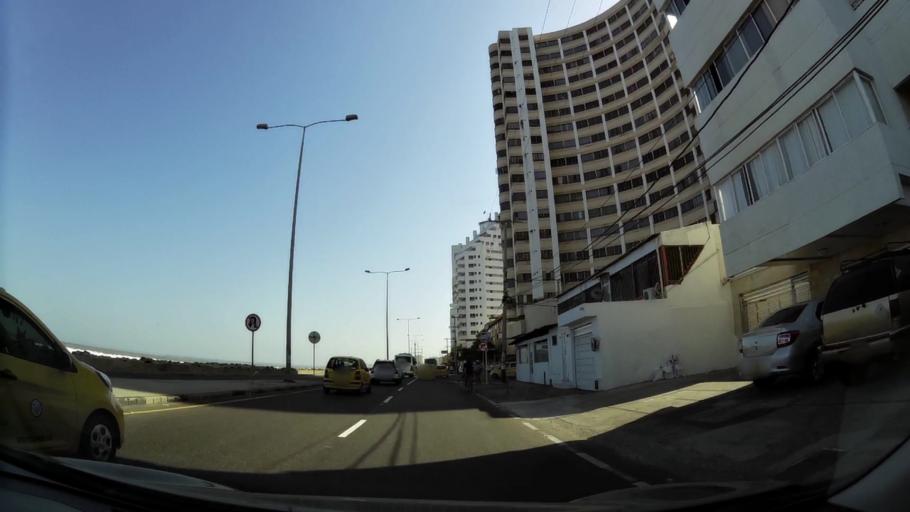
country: CO
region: Bolivar
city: Cartagena
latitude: 10.4355
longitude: -75.5381
